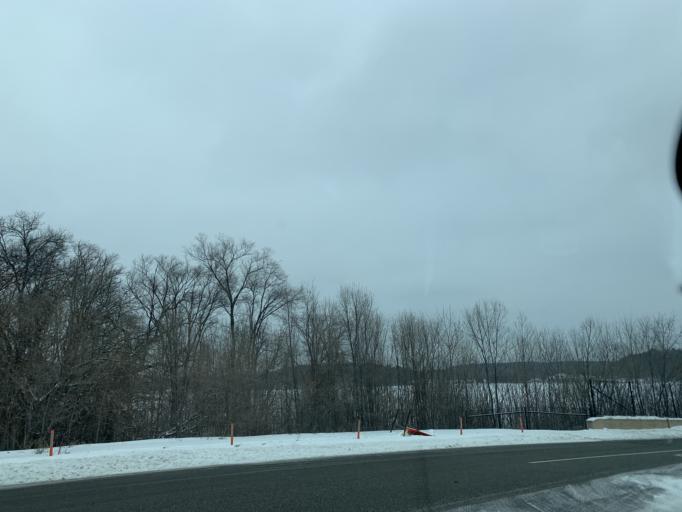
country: US
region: Minnesota
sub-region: Ramsey County
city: Little Canada
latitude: 45.0468
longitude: -93.1054
